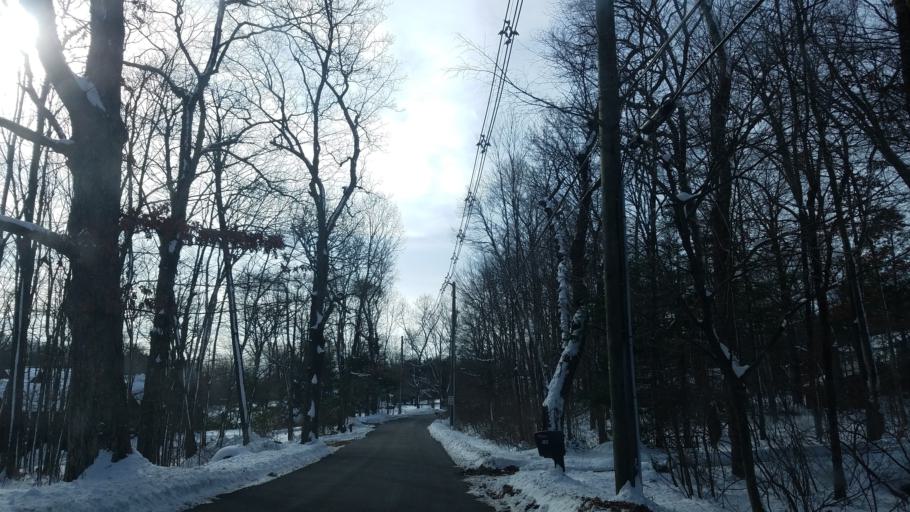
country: US
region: Connecticut
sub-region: Hartford County
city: Canton Valley
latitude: 41.8442
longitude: -72.9077
